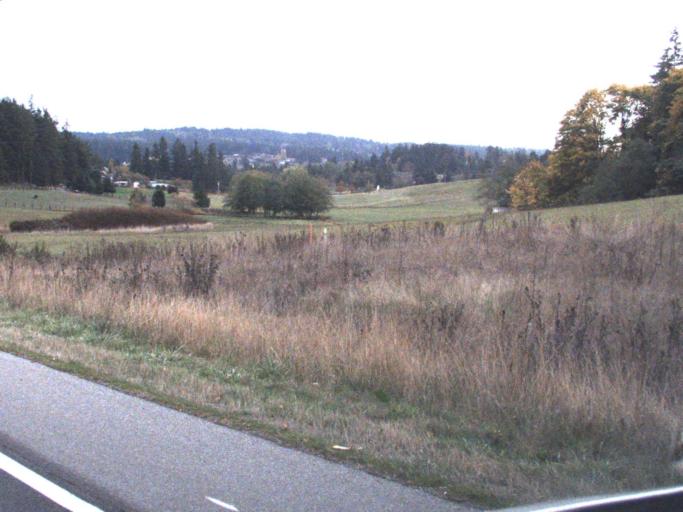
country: US
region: Washington
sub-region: Island County
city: Freeland
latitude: 48.0069
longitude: -122.4925
